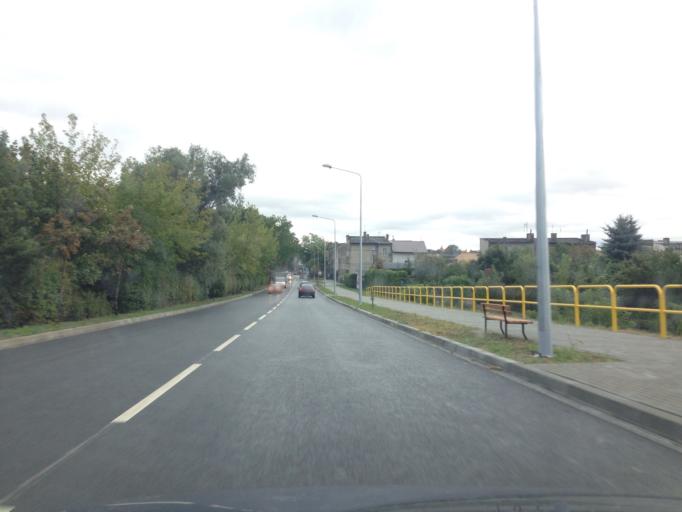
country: PL
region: Kujawsko-Pomorskie
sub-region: Powiat brodnicki
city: Brodnica
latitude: 53.2569
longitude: 19.3972
